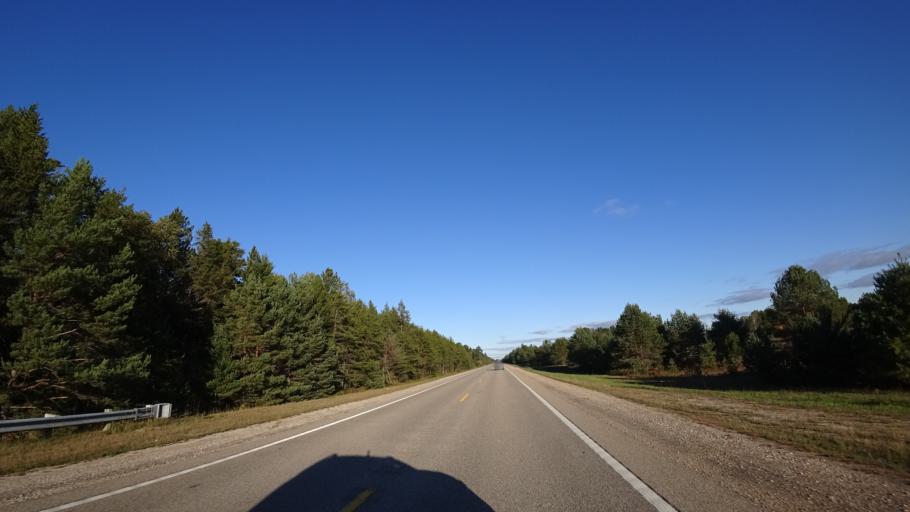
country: US
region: Michigan
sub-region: Schoolcraft County
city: Manistique
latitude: 46.3450
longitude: -85.9900
